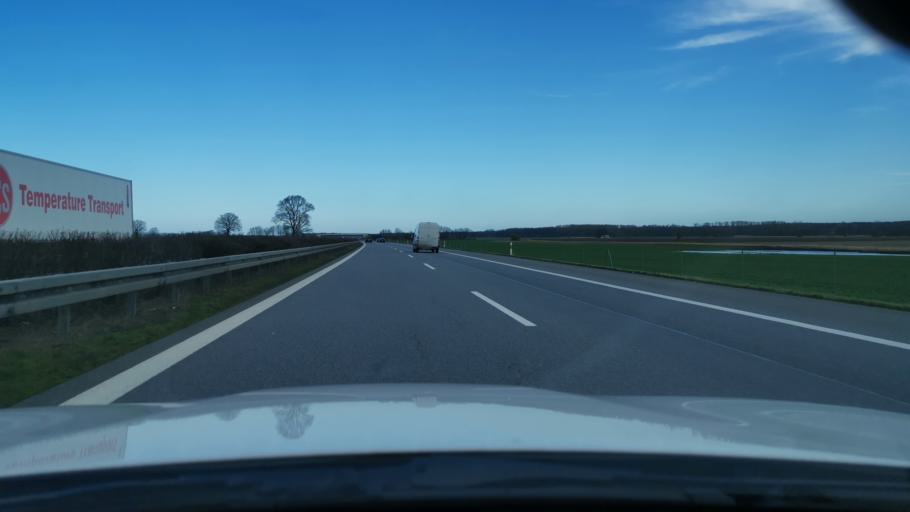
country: DE
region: Brandenburg
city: Wittstock
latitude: 53.2323
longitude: 12.4508
